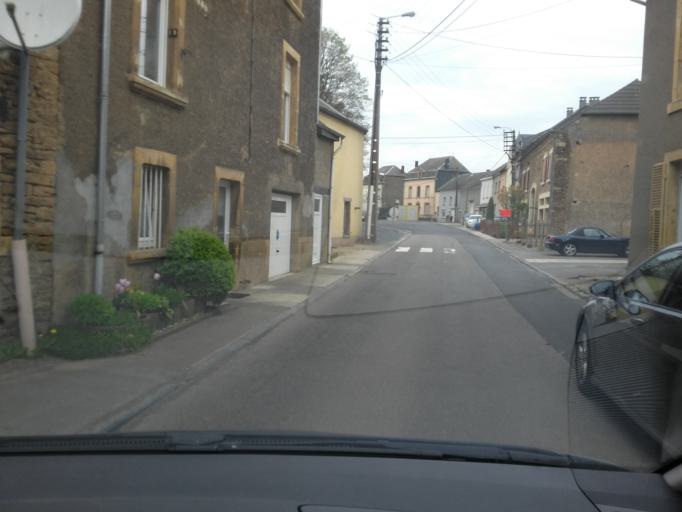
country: BE
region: Wallonia
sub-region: Province du Luxembourg
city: Messancy
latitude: 49.5891
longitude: 5.8172
